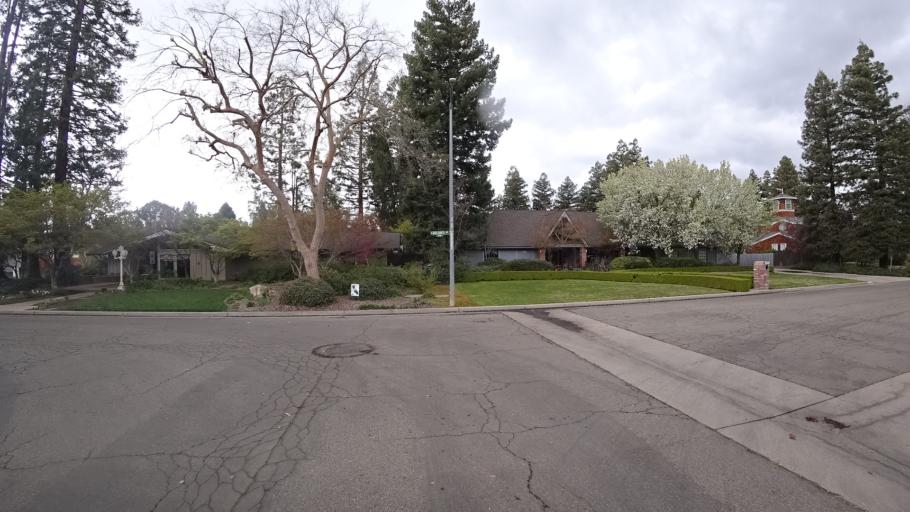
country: US
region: California
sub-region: Fresno County
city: Fresno
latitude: 36.8357
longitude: -119.8292
